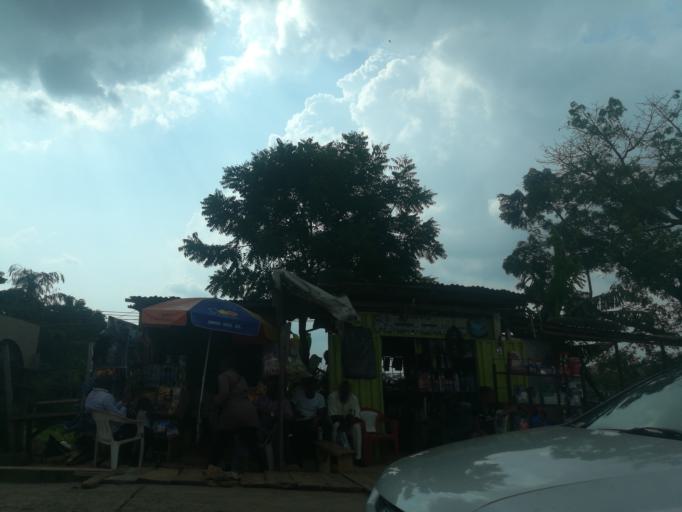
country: NG
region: Oyo
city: Ibadan
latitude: 7.3443
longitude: 3.8774
